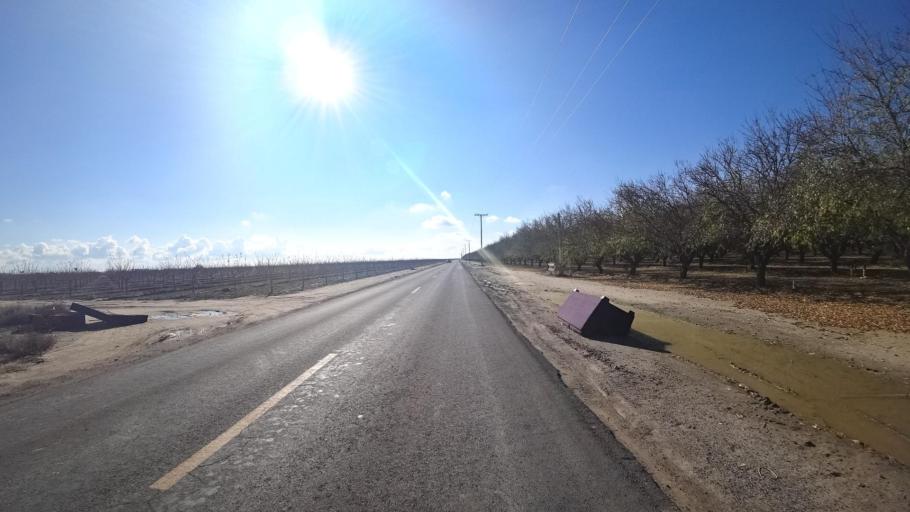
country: US
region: California
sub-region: Kern County
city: Delano
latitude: 35.7381
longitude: -119.2584
